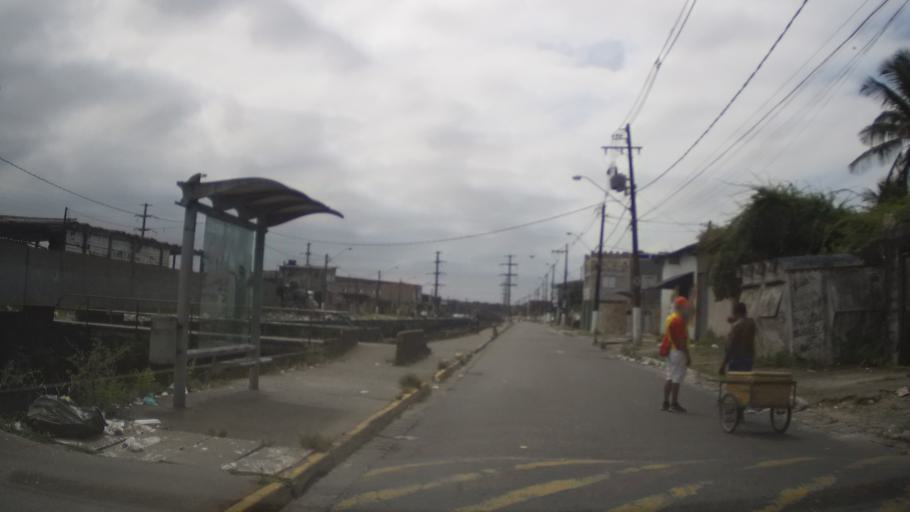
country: BR
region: Sao Paulo
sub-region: Praia Grande
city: Praia Grande
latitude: -24.0182
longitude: -46.4927
